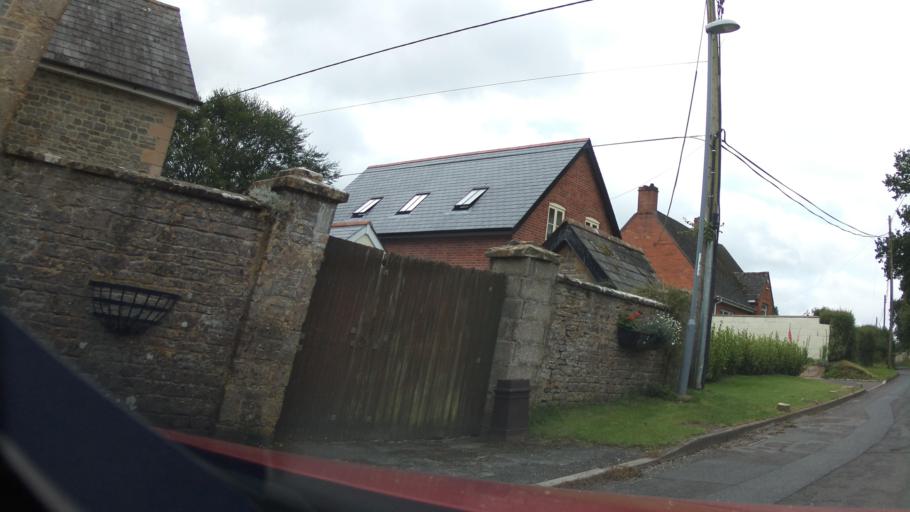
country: GB
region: England
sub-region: Dorset
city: Stalbridge
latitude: 50.9574
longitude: -2.3838
